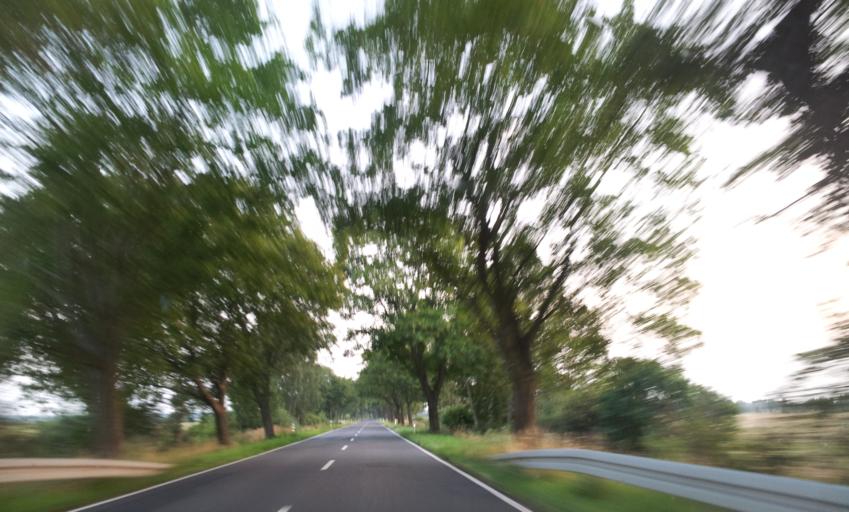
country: DE
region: Brandenburg
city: Treuenbrietzen
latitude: 52.1119
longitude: 12.9639
